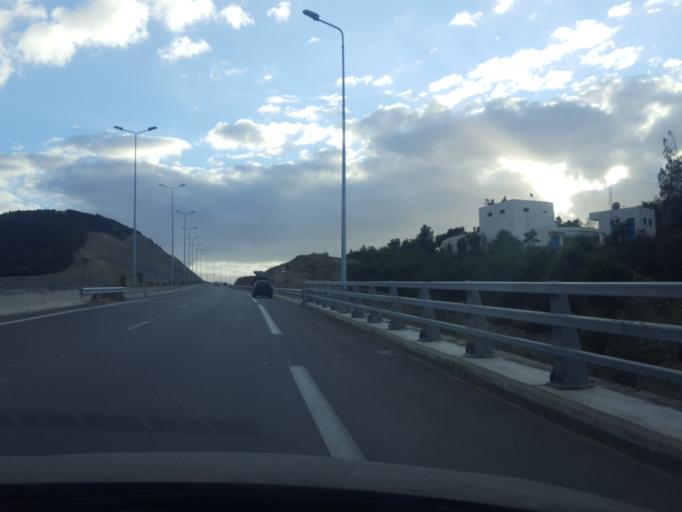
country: TN
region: Tunis
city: Hammam-Lif
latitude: 36.6965
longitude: 10.3989
